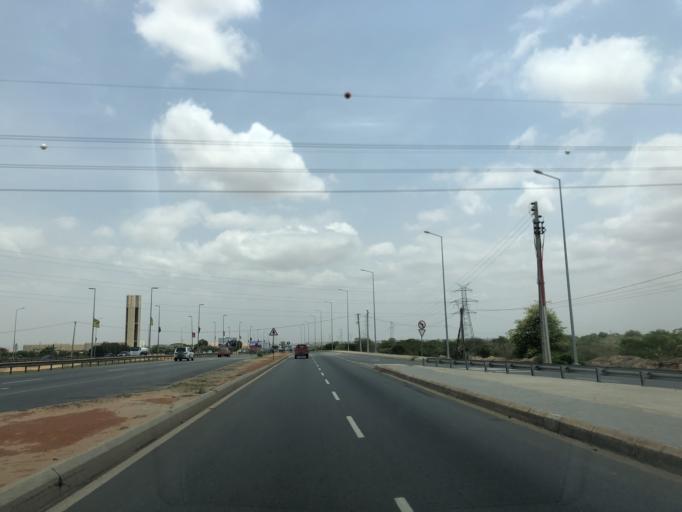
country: AO
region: Luanda
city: Luanda
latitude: -8.9737
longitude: 13.2558
